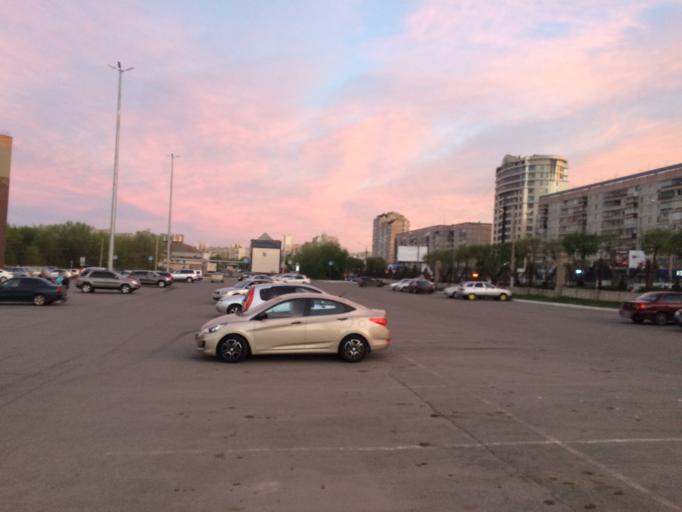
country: RU
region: Chelyabinsk
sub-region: Gorod Magnitogorsk
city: Magnitogorsk
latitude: 53.4029
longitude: 58.9864
